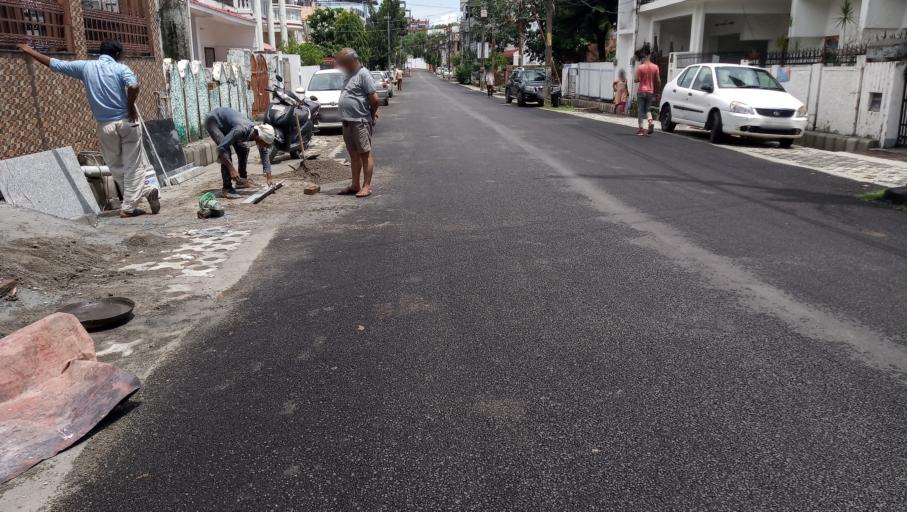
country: IN
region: Uttarakhand
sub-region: Dehradun
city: Dehradun
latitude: 30.3656
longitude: 78.0650
